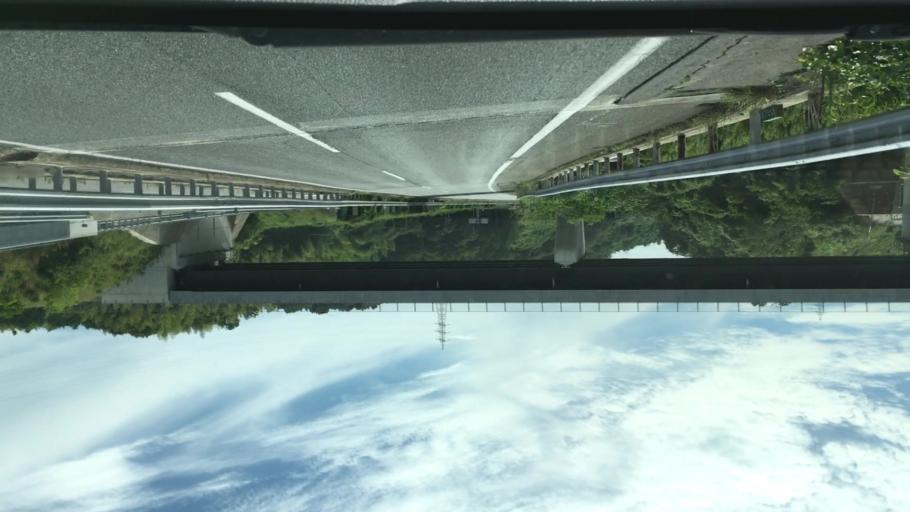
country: JP
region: Yamaguchi
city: Ogori-shimogo
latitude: 34.1264
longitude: 131.4040
